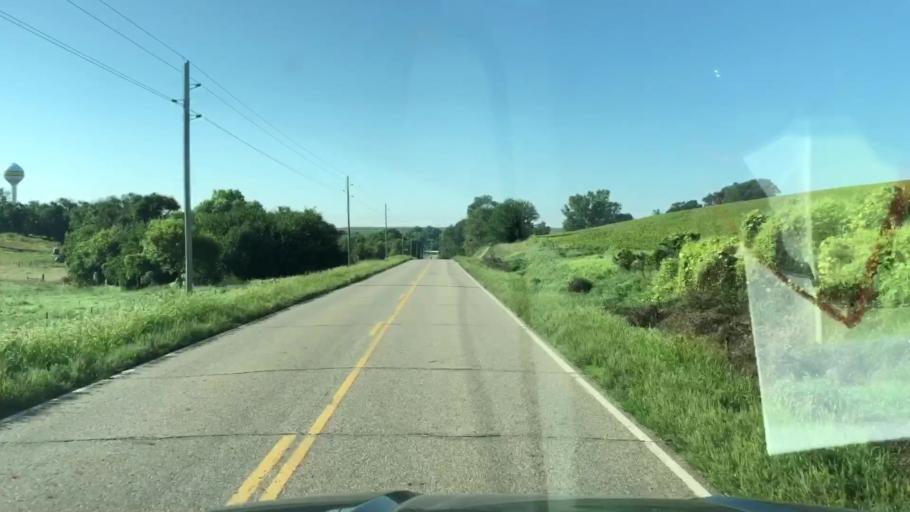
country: US
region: Iowa
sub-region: Woodbury County
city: Sergeant Bluff
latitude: 42.4152
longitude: -96.2138
